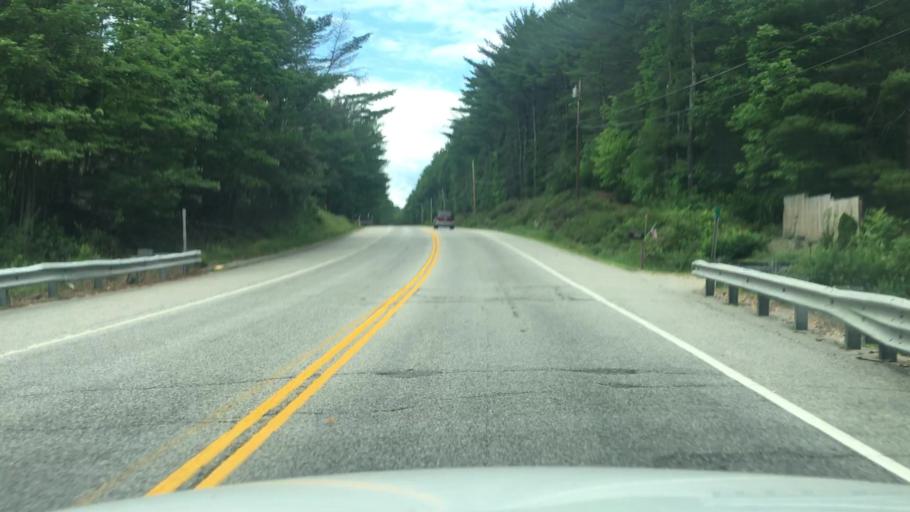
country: US
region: Maine
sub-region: Oxford County
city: West Paris
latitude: 44.3379
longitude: -70.5576
